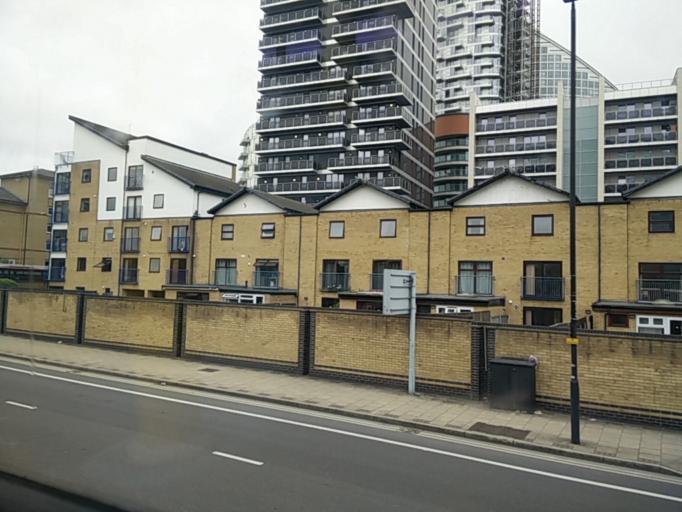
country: GB
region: England
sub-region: Greater London
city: Poplar
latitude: 51.5061
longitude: -0.0075
